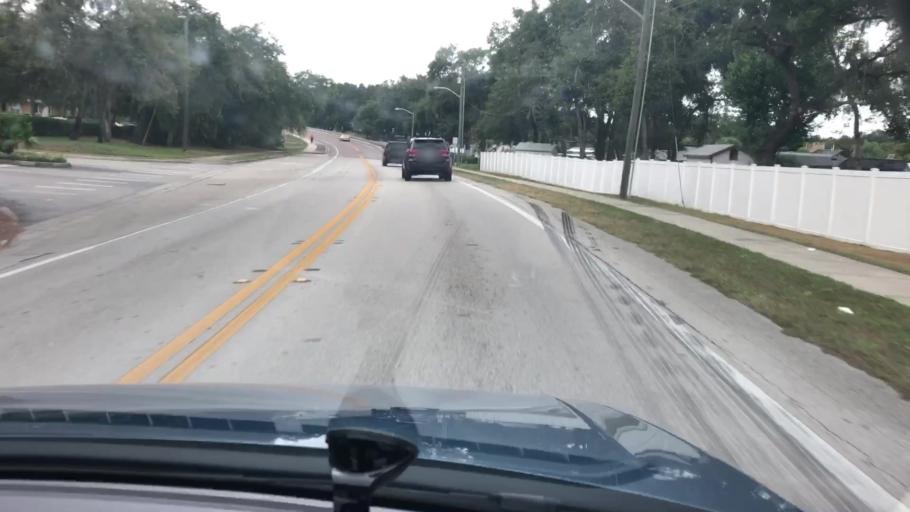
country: US
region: Florida
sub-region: Polk County
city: Gibsonia
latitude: 28.1088
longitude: -81.9389
